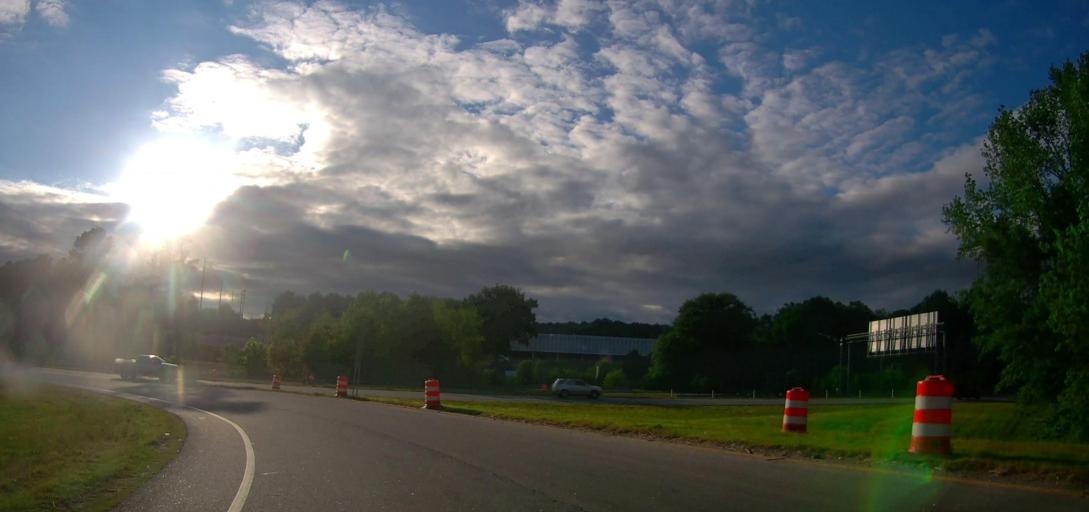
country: US
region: Georgia
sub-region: Clarke County
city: Athens
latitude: 33.9790
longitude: -83.3505
